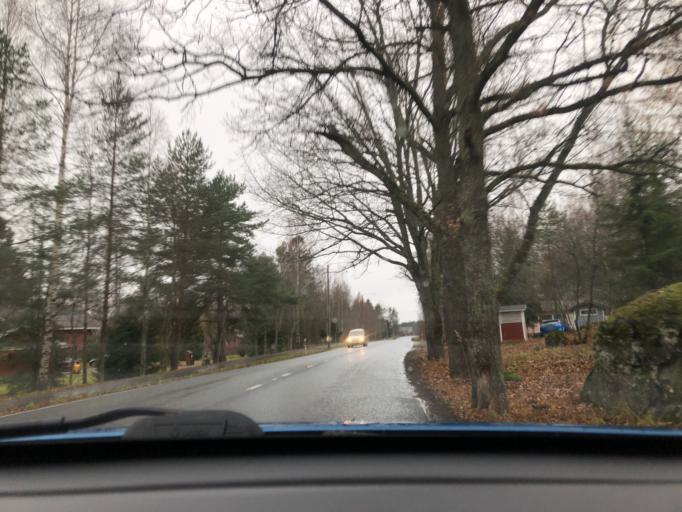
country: FI
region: Pirkanmaa
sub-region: Tampere
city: Kangasala
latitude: 61.4525
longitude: 24.0322
